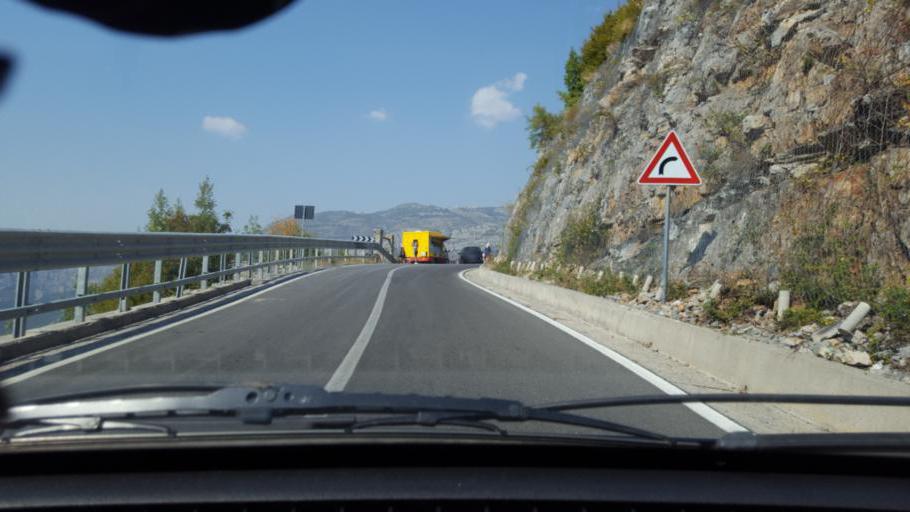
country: AL
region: Shkoder
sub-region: Rrethi i Malesia e Madhe
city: Kastrat
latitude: 42.4145
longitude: 19.5037
